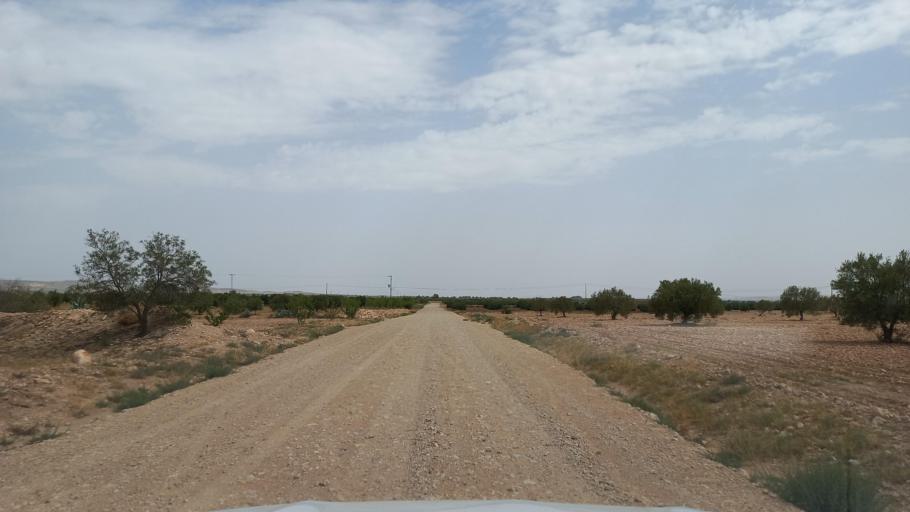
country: TN
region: Al Qasrayn
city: Kasserine
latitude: 35.2787
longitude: 9.0163
